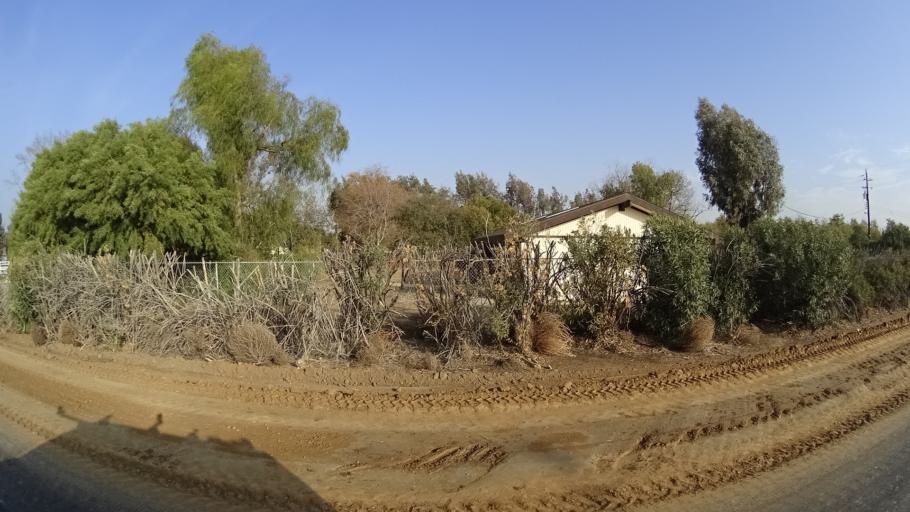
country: US
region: California
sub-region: Kern County
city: Greenacres
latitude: 35.4343
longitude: -119.1014
